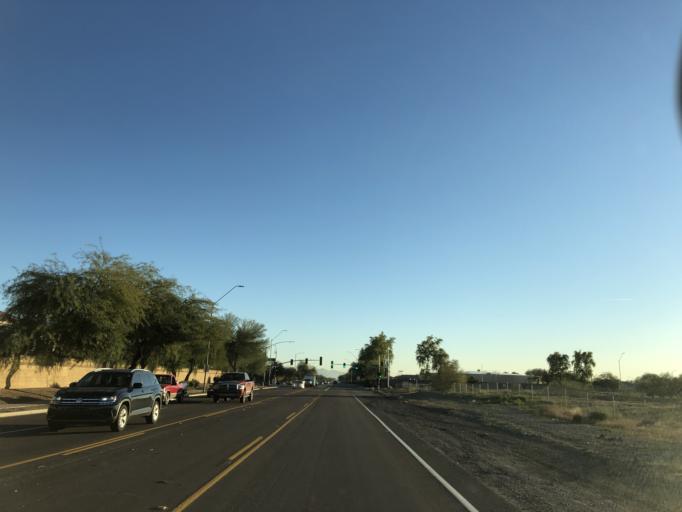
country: US
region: Arizona
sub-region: Maricopa County
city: Sun City West
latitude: 33.6906
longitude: -112.2898
